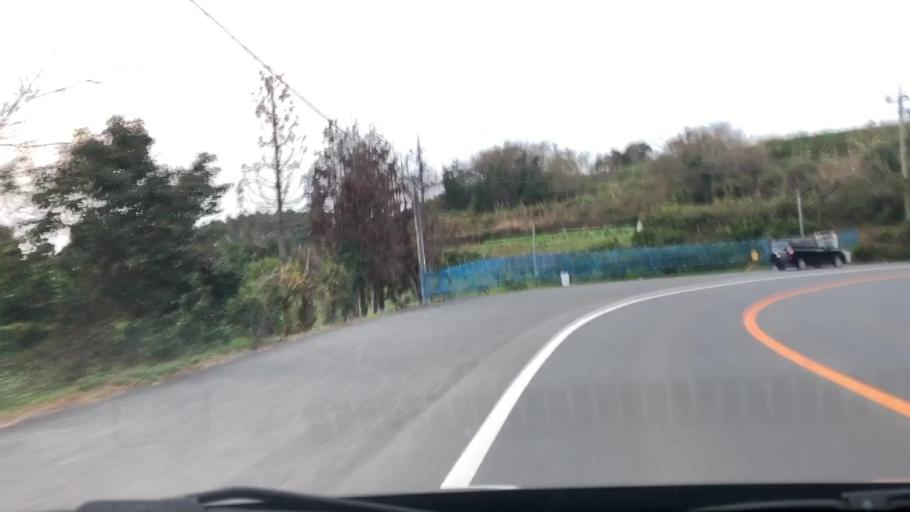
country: JP
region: Nagasaki
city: Sasebo
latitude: 33.0452
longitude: 129.7078
